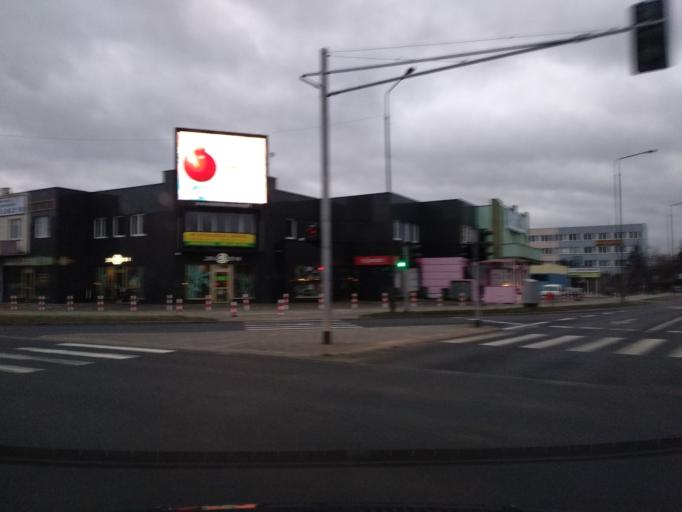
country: PL
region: Greater Poland Voivodeship
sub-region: Konin
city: Konin
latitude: 52.2295
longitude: 18.2450
